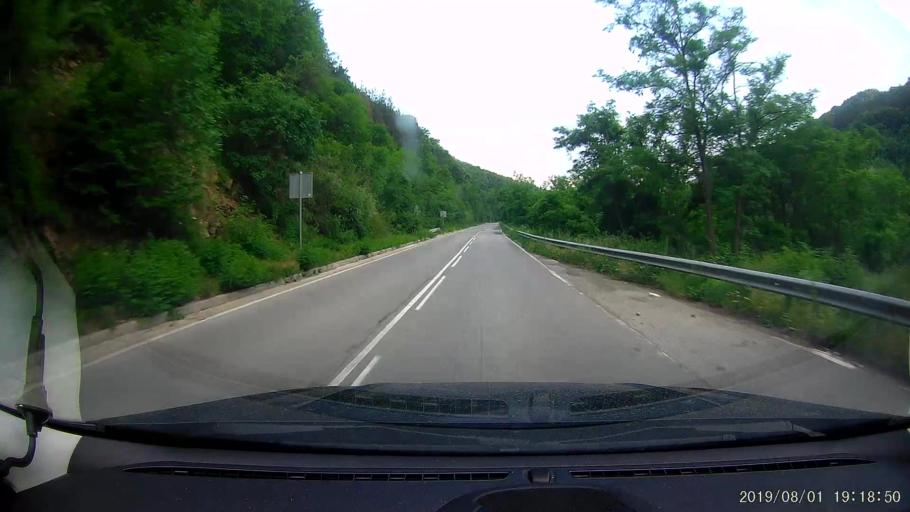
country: BG
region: Shumen
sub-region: Obshtina Smyadovo
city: Smyadovo
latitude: 42.9074
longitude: 26.9403
